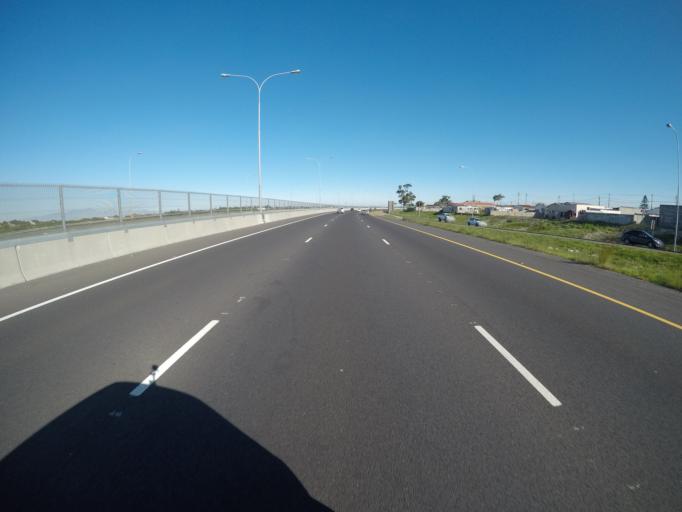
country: ZA
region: Western Cape
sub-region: City of Cape Town
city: Kraaifontein
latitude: -33.9804
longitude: 18.6520
